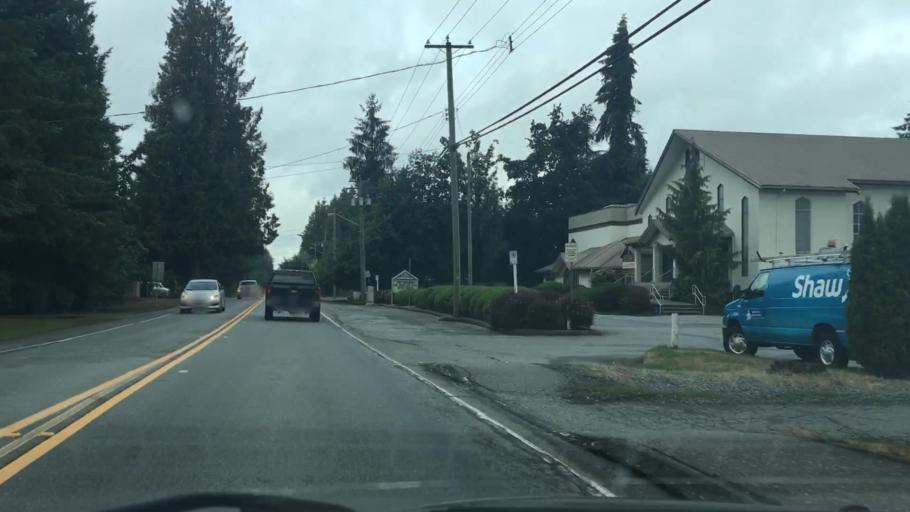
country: CA
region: British Columbia
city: Langley
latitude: 49.1041
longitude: -122.5393
